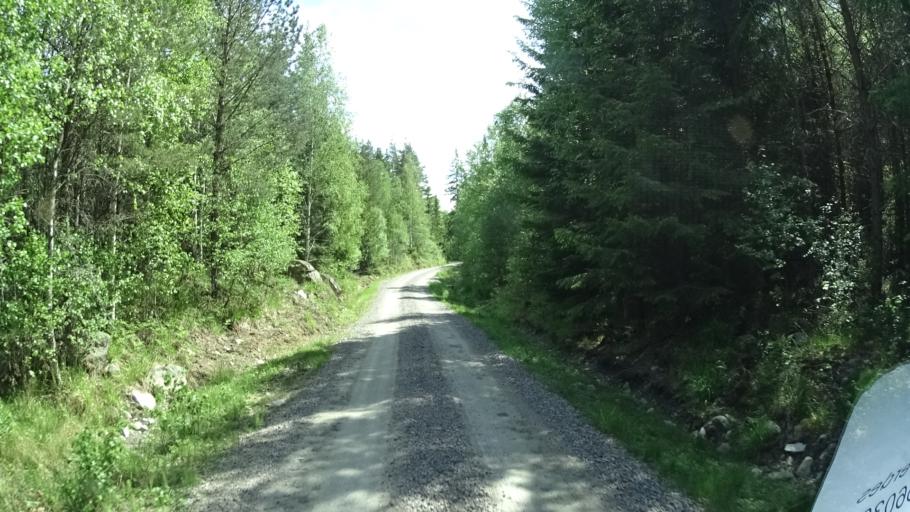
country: SE
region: OEstergoetland
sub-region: Finspangs Kommun
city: Finspang
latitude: 58.7855
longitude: 15.9011
